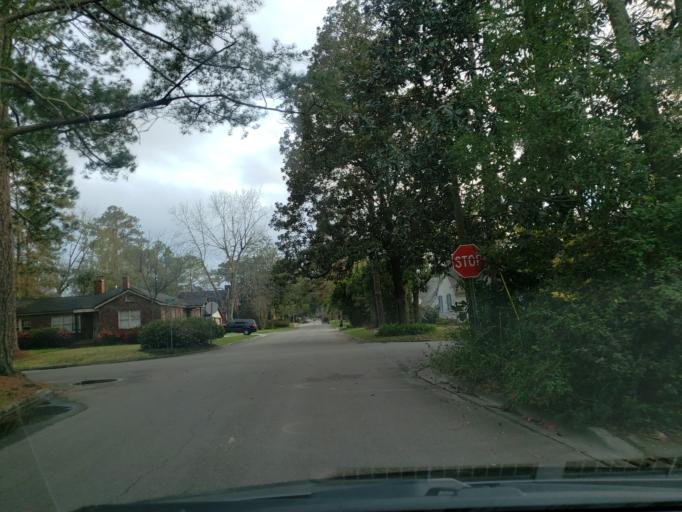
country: US
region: Georgia
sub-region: Chatham County
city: Savannah
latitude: 32.0391
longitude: -81.0954
